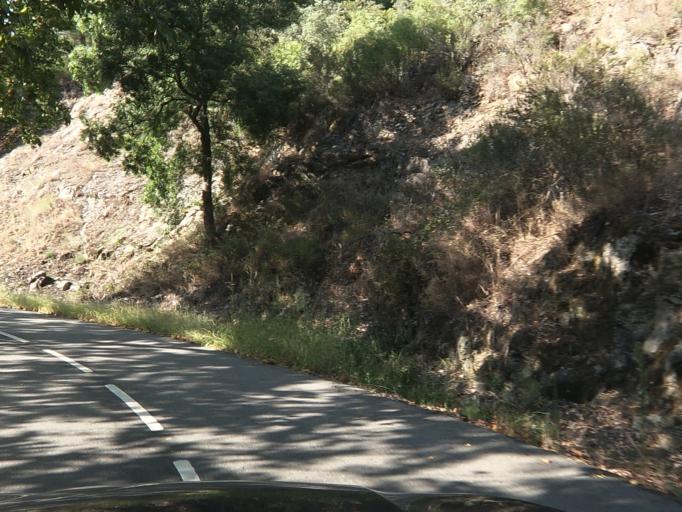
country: PT
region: Vila Real
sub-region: Sabrosa
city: Vilela
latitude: 41.2038
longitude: -7.6227
